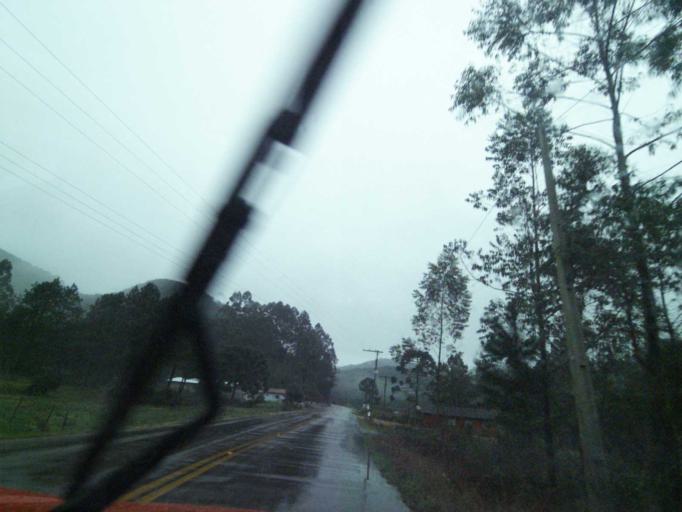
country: BR
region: Santa Catarina
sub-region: Anitapolis
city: Anitapolis
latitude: -27.8428
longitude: -49.0516
